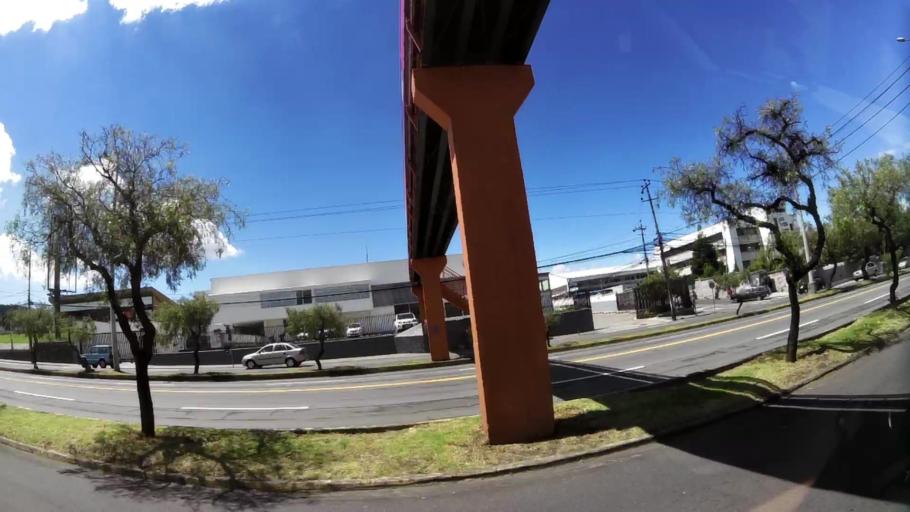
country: EC
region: Pichincha
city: Quito
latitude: -0.1284
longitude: -78.4812
